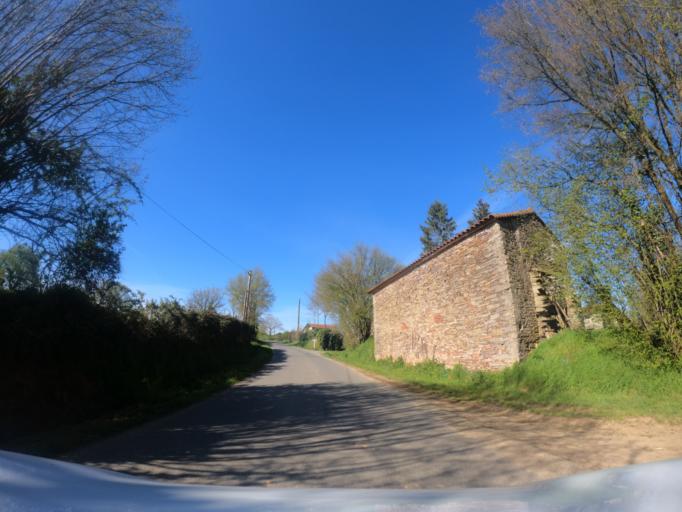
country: FR
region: Pays de la Loire
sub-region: Departement de la Vendee
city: La Tardiere
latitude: 46.6895
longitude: -0.7389
